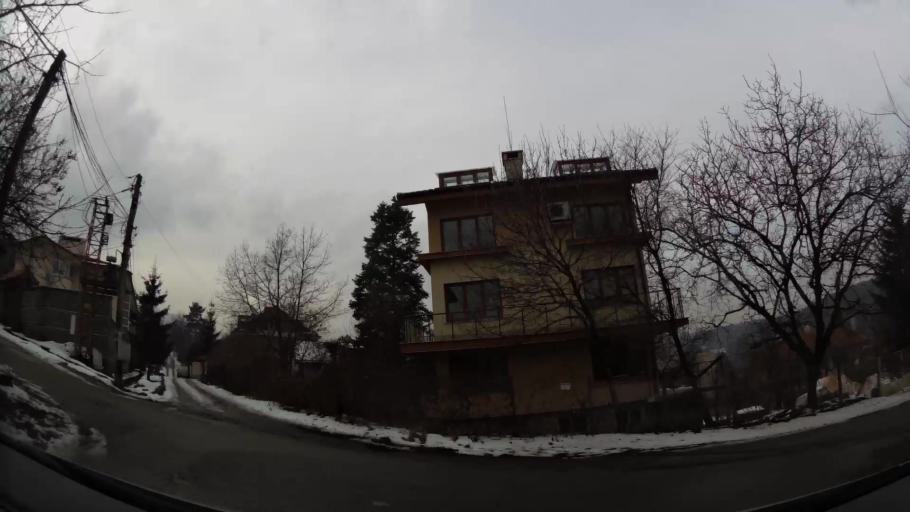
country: BG
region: Sofia-Capital
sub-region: Stolichna Obshtina
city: Sofia
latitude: 42.6539
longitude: 23.2361
